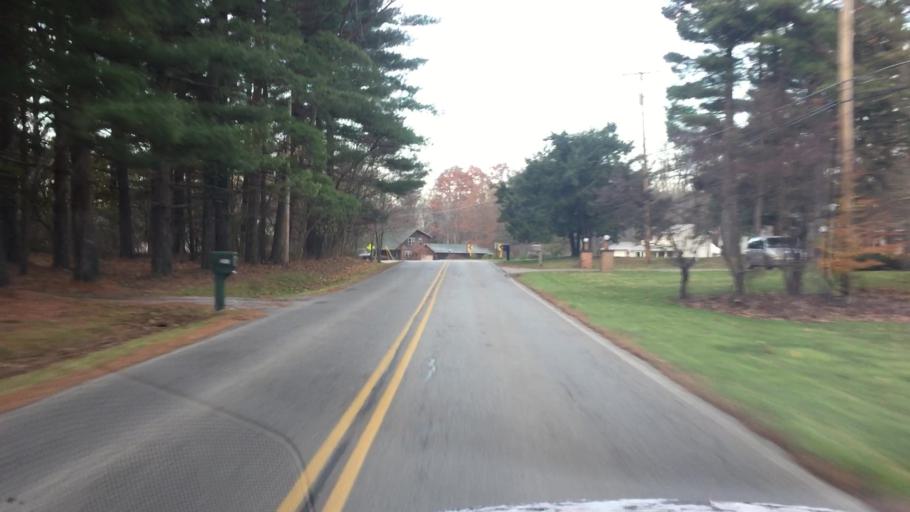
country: US
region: Ohio
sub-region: Mahoning County
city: Poland
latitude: 41.0051
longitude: -80.6169
